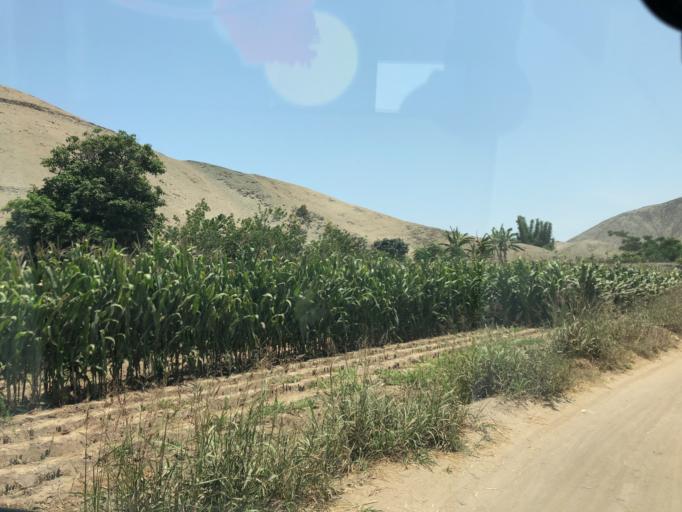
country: PE
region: Lima
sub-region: Provincia de Canete
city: Quilmana
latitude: -12.9979
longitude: -76.4460
